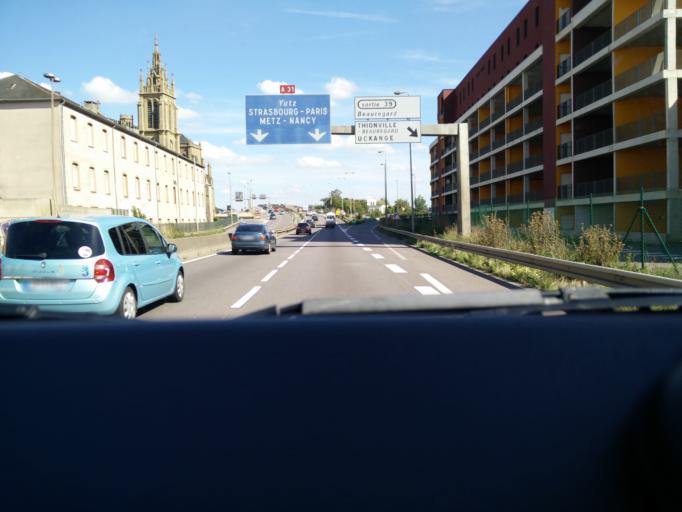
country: FR
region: Lorraine
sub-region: Departement de la Moselle
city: Terville
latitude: 49.3491
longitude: 6.1538
